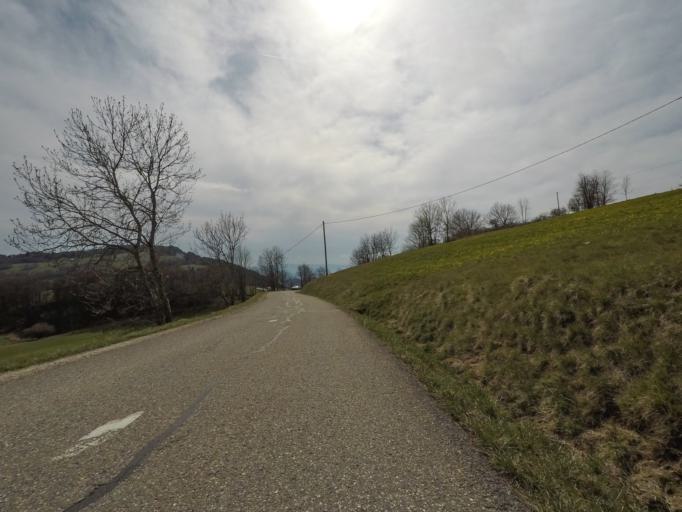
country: FR
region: Rhone-Alpes
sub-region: Departement de la Haute-Savoie
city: Collonges-sous-Saleve
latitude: 46.1265
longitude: 6.1745
